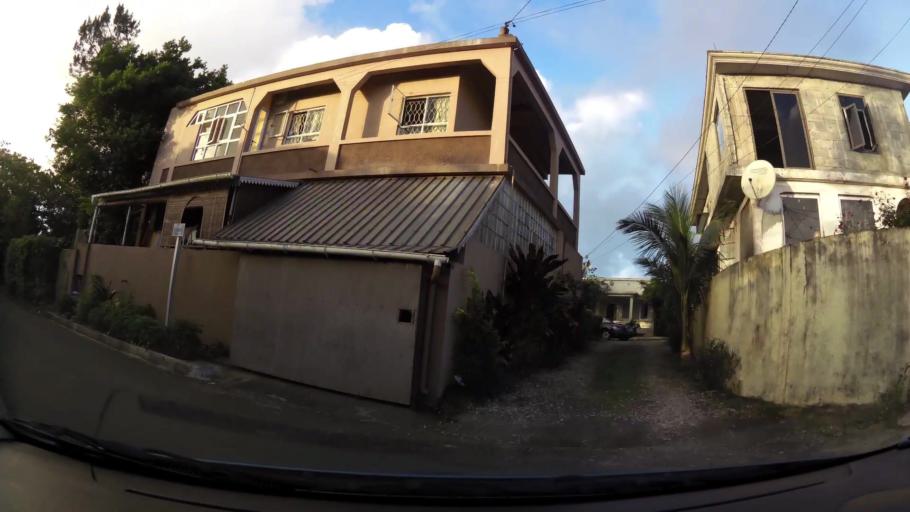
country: MU
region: Plaines Wilhems
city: Curepipe
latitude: -20.3094
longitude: 57.5306
